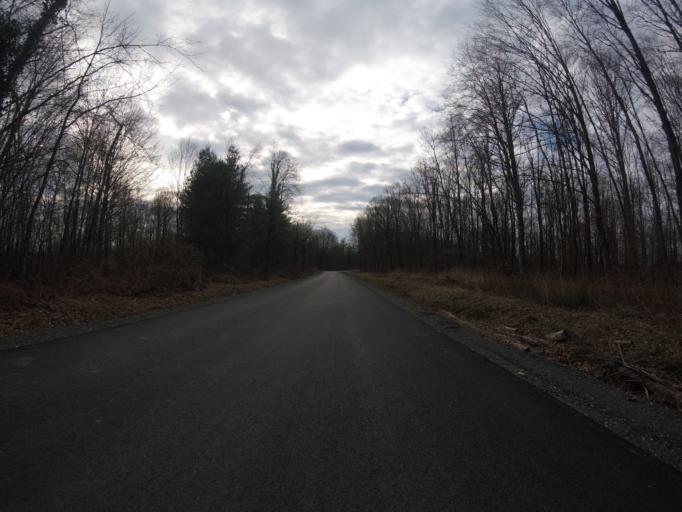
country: HR
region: Sisacko-Moslavacka
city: Glina
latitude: 45.4959
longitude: 16.0456
